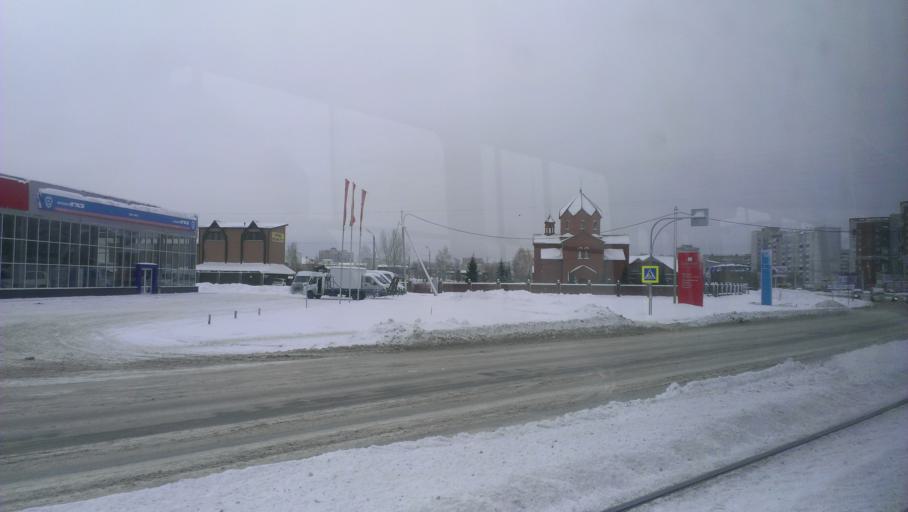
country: RU
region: Altai Krai
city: Novosilikatnyy
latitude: 53.3308
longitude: 83.6662
